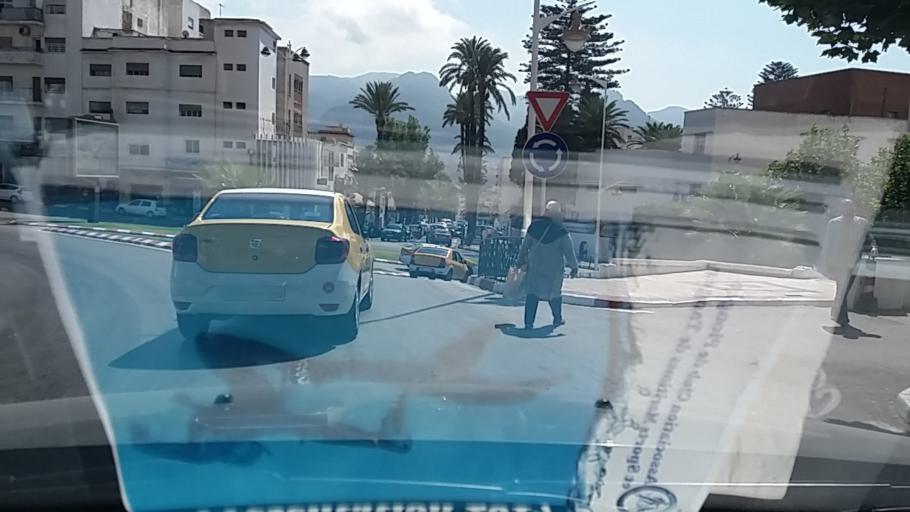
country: MA
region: Tanger-Tetouan
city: Tetouan
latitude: 35.5735
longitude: -5.3796
